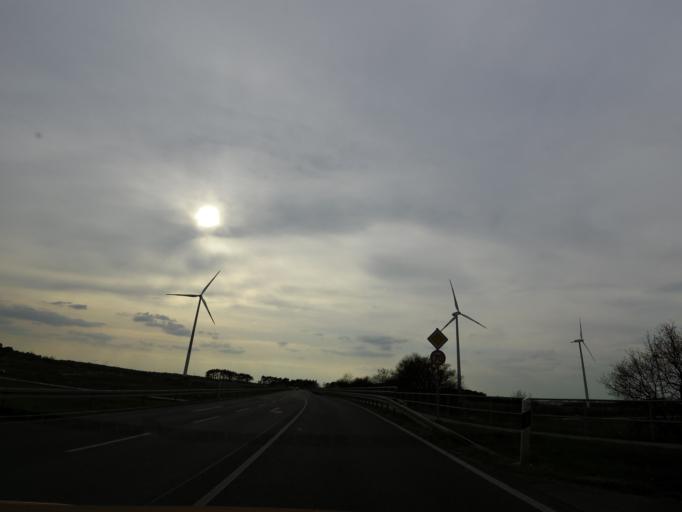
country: DE
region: Brandenburg
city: Mittenwalde
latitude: 52.2461
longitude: 13.5909
